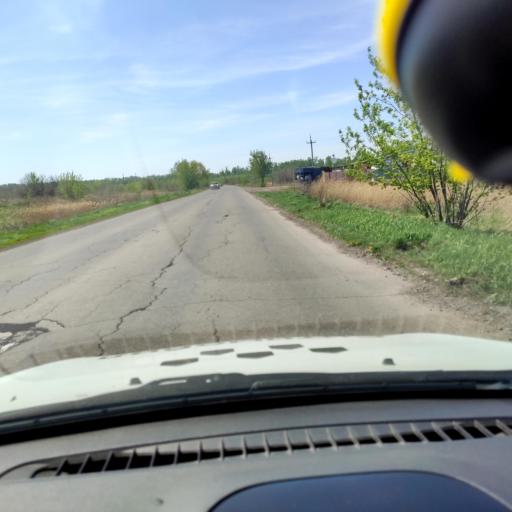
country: RU
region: Samara
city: Tol'yatti
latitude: 53.6392
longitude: 49.3138
